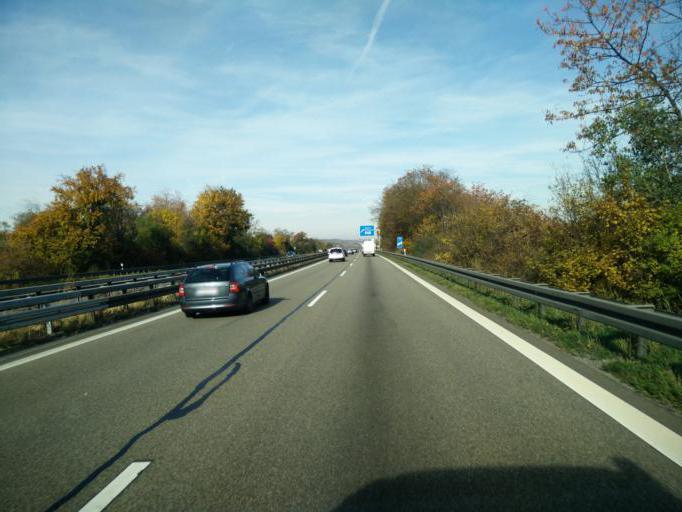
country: DE
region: Baden-Wuerttemberg
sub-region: Karlsruhe Region
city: Niefern-Oschelbronn
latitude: 48.9038
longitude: 8.7775
